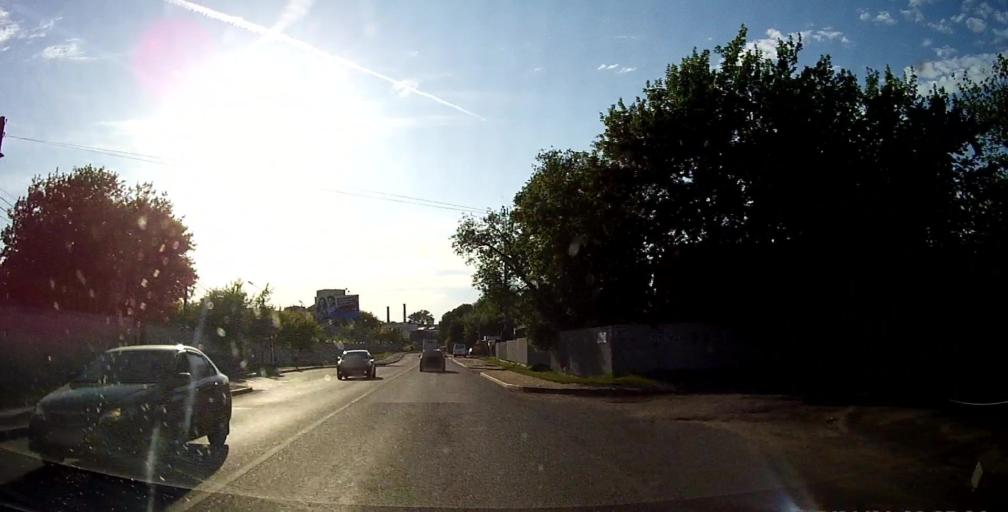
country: RU
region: Moskovskaya
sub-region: Podol'skiy Rayon
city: Podol'sk
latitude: 55.4352
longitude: 37.5879
